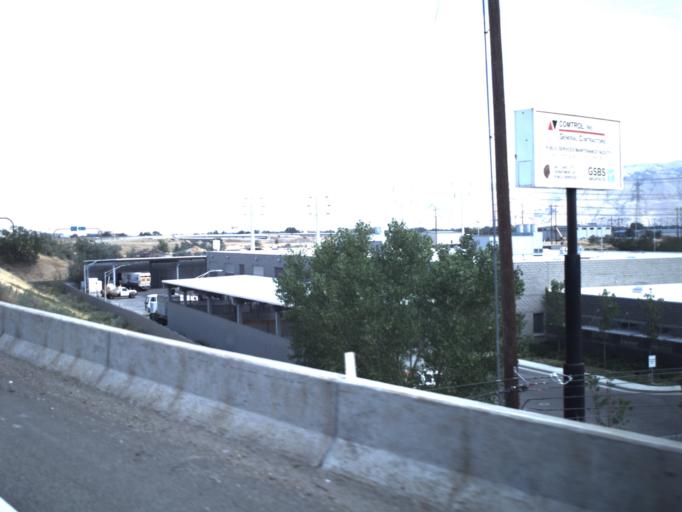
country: US
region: Utah
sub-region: Salt Lake County
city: Salt Lake City
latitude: 40.7584
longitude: -111.9500
